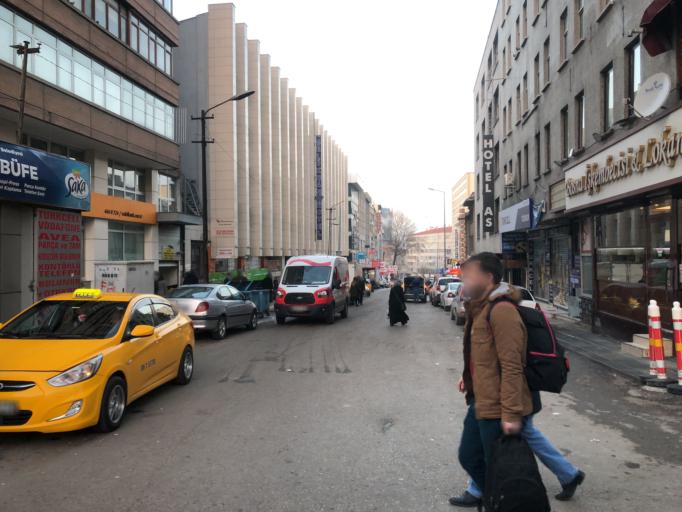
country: TR
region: Ankara
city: Ankara
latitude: 39.9431
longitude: 32.8545
